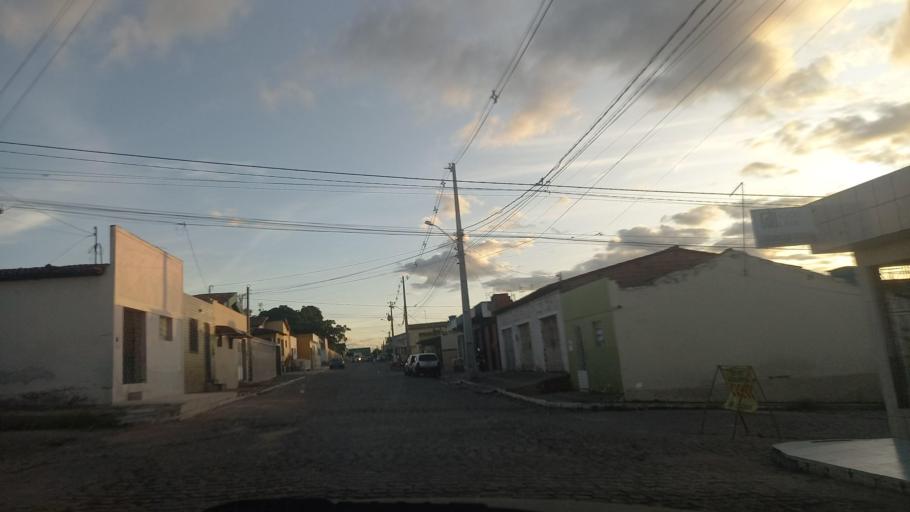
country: BR
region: Pernambuco
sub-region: Bezerros
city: Bezerros
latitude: -8.2395
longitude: -35.7500
